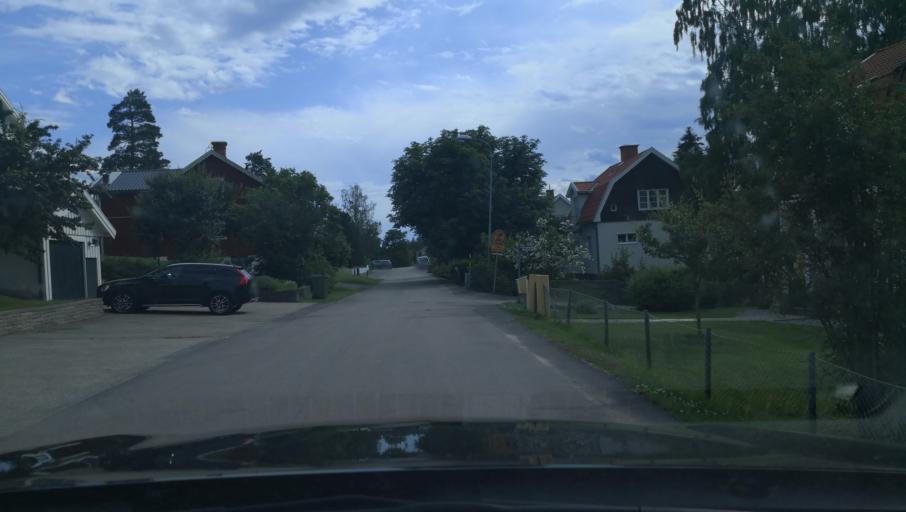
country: SE
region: Vaestmanland
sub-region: Fagersta Kommun
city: Fagersta
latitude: 59.9877
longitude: 15.8280
